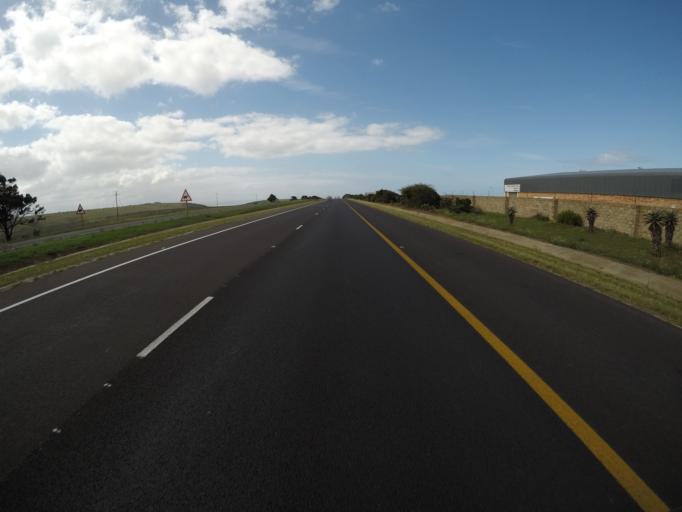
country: ZA
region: Western Cape
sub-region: Eden District Municipality
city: Mossel Bay
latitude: -34.1703
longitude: 22.0760
